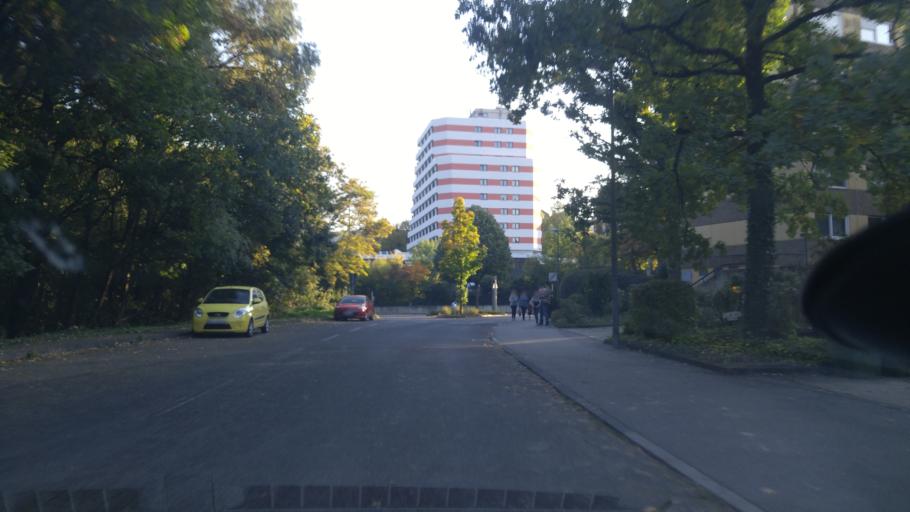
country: DE
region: Baden-Wuerttemberg
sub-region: Regierungsbezirk Stuttgart
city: Stuttgart Feuerbach
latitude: 48.7802
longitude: 9.1336
